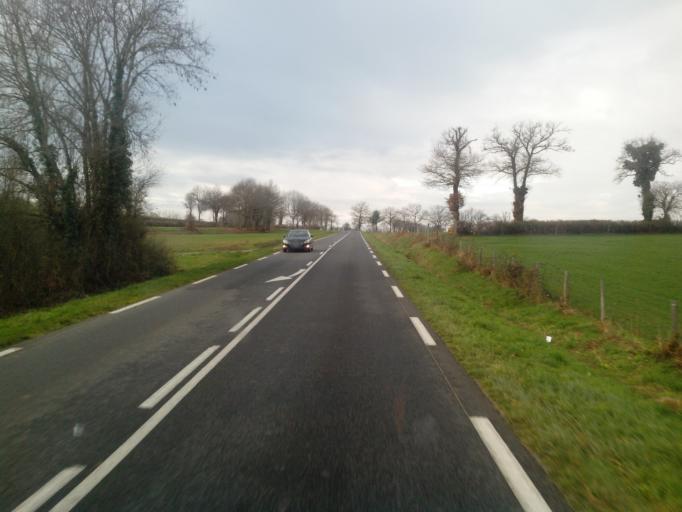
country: FR
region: Limousin
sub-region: Departement de la Haute-Vienne
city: Le Dorat
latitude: 46.2146
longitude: 1.1150
